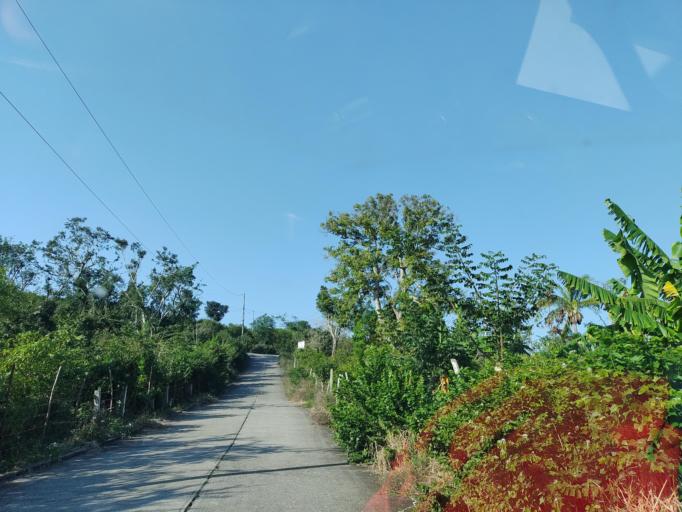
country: MX
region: Veracruz
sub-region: Papantla
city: Polutla
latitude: 20.4577
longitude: -97.2266
